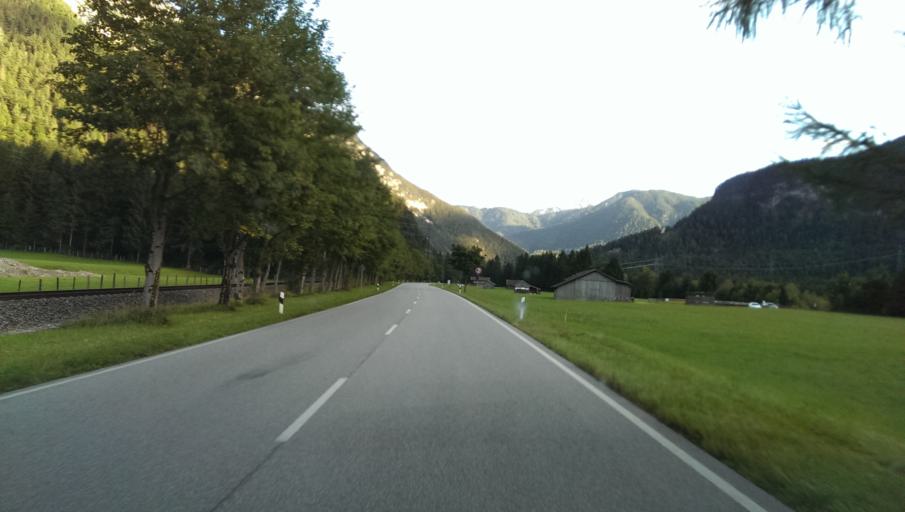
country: AT
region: Tyrol
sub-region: Politischer Bezirk Innsbruck Land
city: Scharnitz
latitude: 47.4100
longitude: 11.2591
